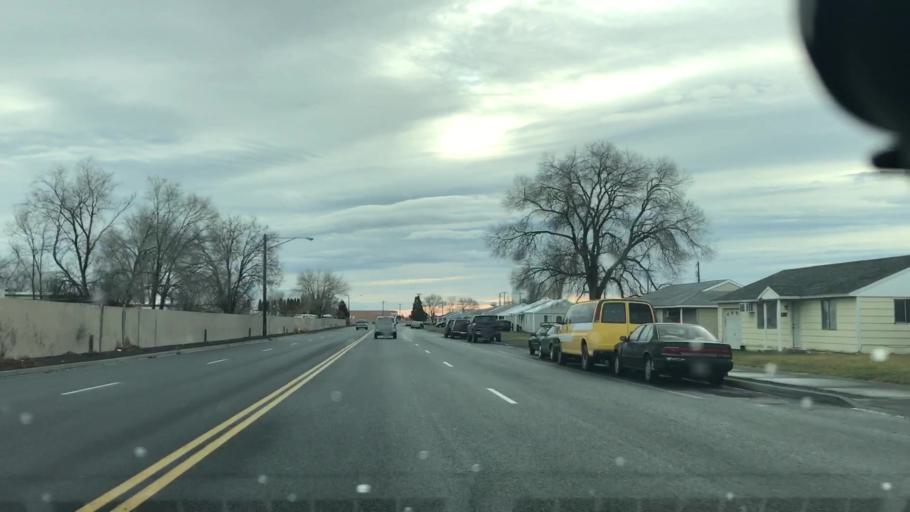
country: US
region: Washington
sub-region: Grant County
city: Moses Lake North
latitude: 47.1771
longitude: -119.3216
